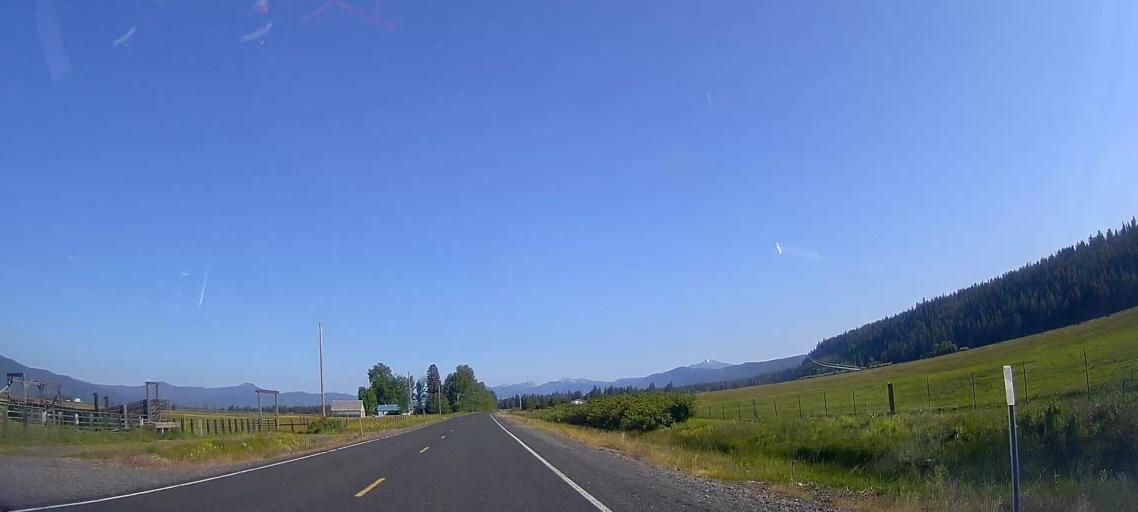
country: US
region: Oregon
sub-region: Klamath County
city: Klamath Falls
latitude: 42.6610
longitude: -121.9636
